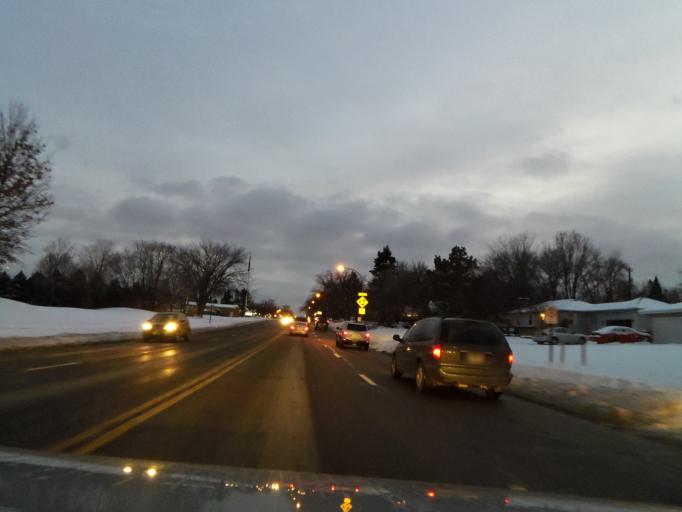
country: US
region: Minnesota
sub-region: Hennepin County
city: Richfield
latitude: 44.8869
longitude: -93.2679
